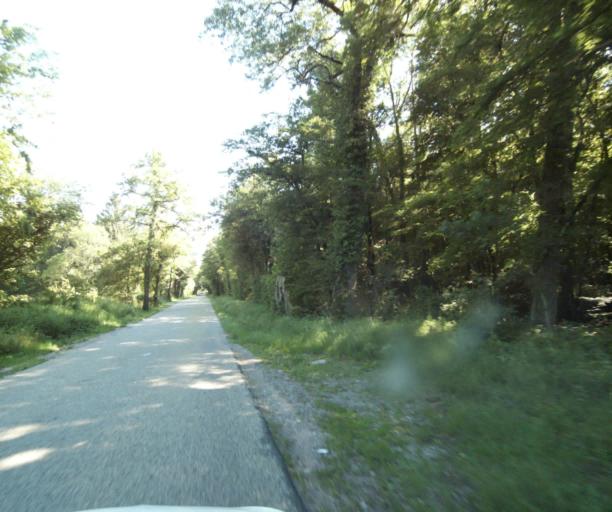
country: FR
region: Rhone-Alpes
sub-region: Departement de la Haute-Savoie
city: Ballaison
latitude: 46.2889
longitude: 6.3478
